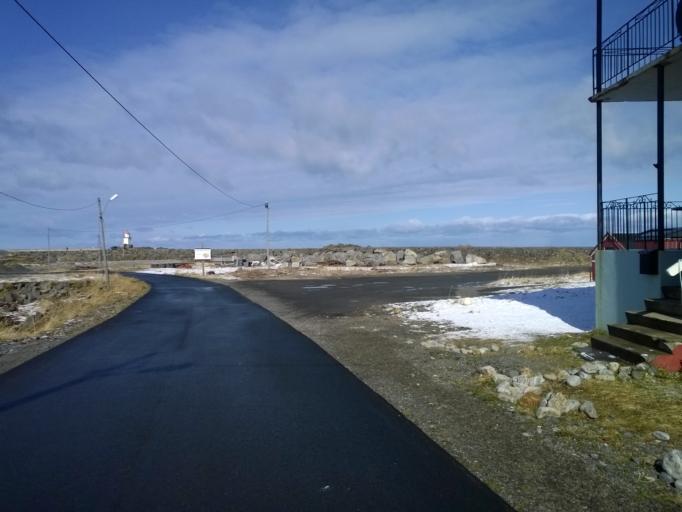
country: NO
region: Nordland
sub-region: Vagan
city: Kabelvag
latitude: 68.3894
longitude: 14.4138
